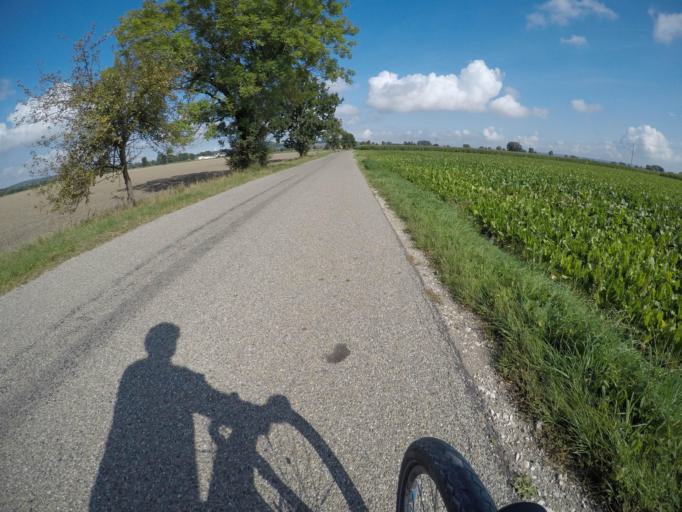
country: DE
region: Bavaria
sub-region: Swabia
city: Tapfheim
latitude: 48.6590
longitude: 10.7281
